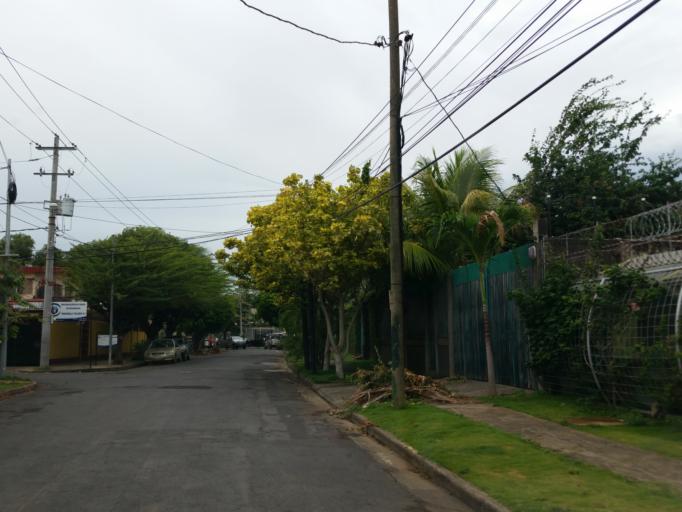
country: NI
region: Managua
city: Managua
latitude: 12.1374
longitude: -86.2809
